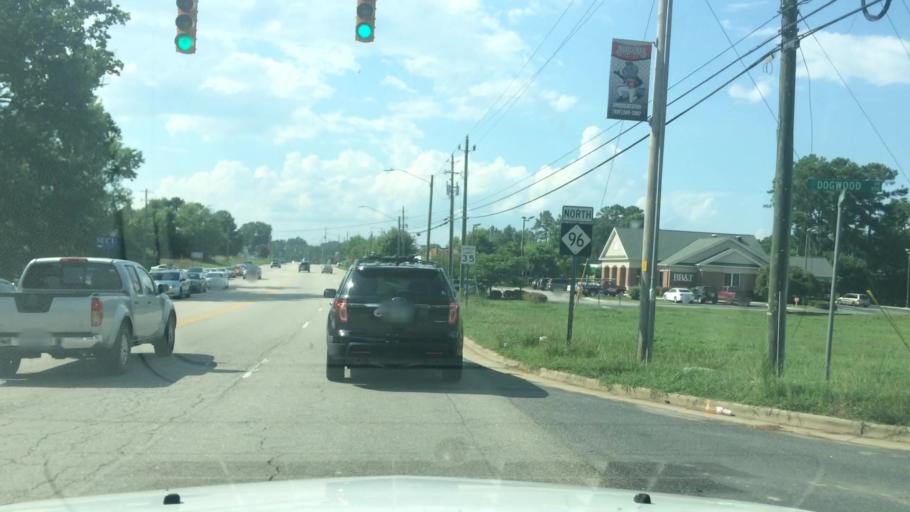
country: US
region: North Carolina
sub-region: Wake County
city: Zebulon
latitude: 35.8361
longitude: -78.3223
